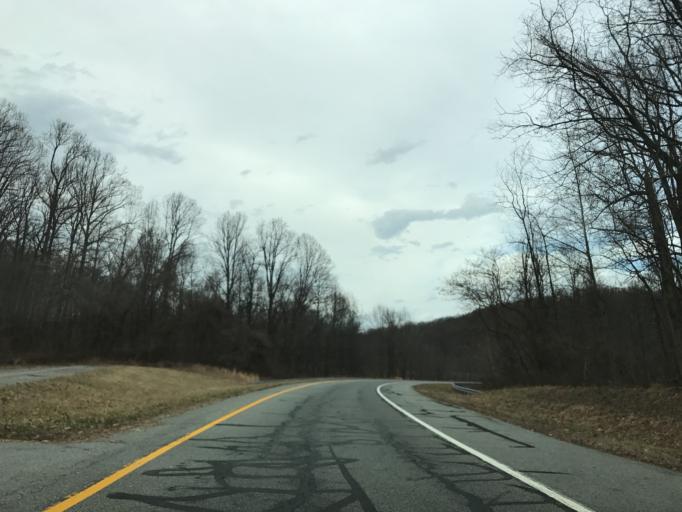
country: US
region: Maryland
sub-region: Harford County
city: North Bel Air
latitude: 39.5307
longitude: -76.3662
